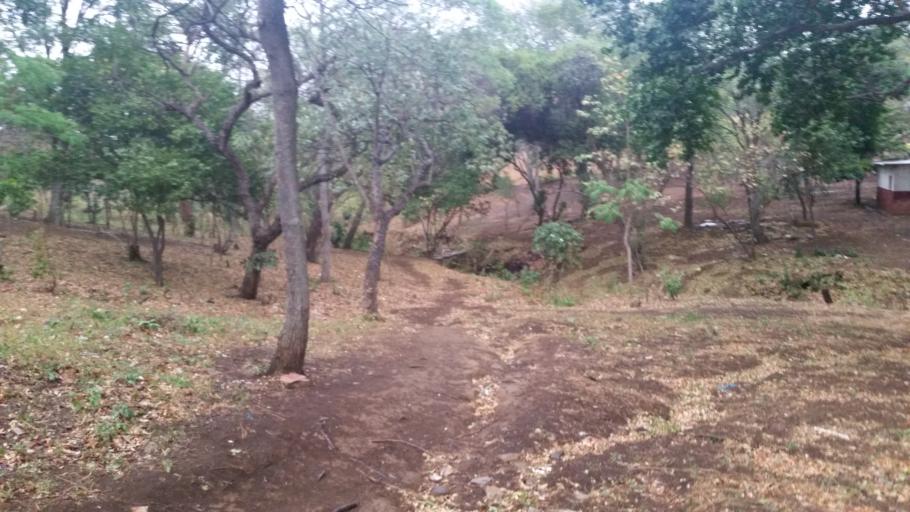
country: NI
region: Managua
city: Managua
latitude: 12.0903
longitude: -86.2560
